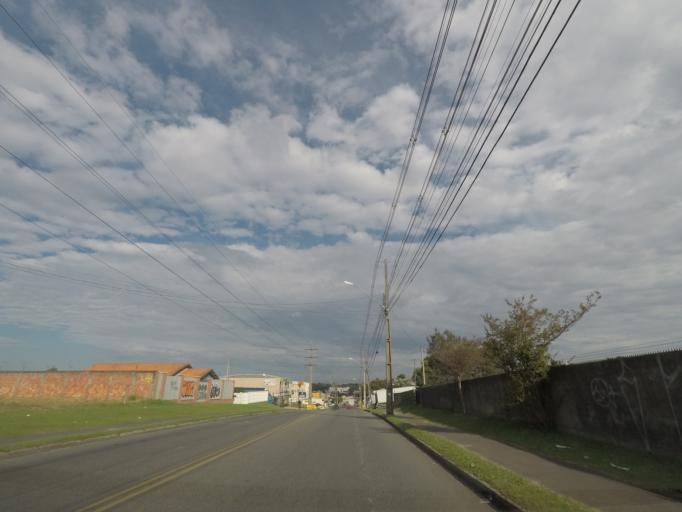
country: BR
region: Parana
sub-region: Sao Jose Dos Pinhais
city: Sao Jose dos Pinhais
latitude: -25.5489
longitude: -49.2932
